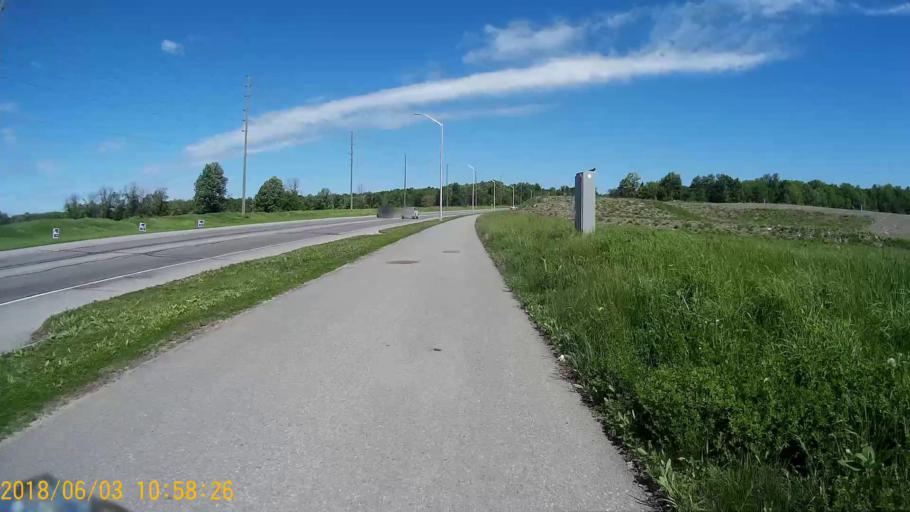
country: CA
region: Ontario
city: Bells Corners
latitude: 45.3197
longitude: -75.9460
